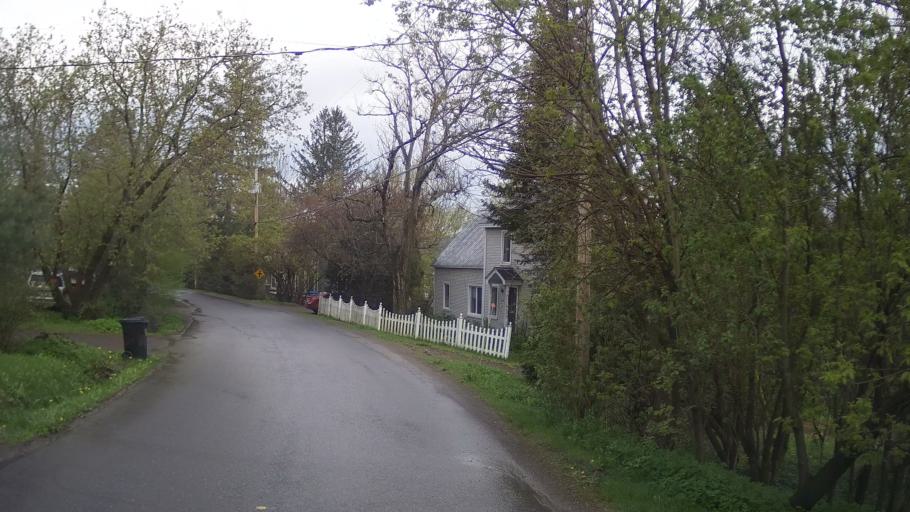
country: CA
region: Quebec
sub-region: Monteregie
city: Sutton
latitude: 45.1758
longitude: -72.6591
